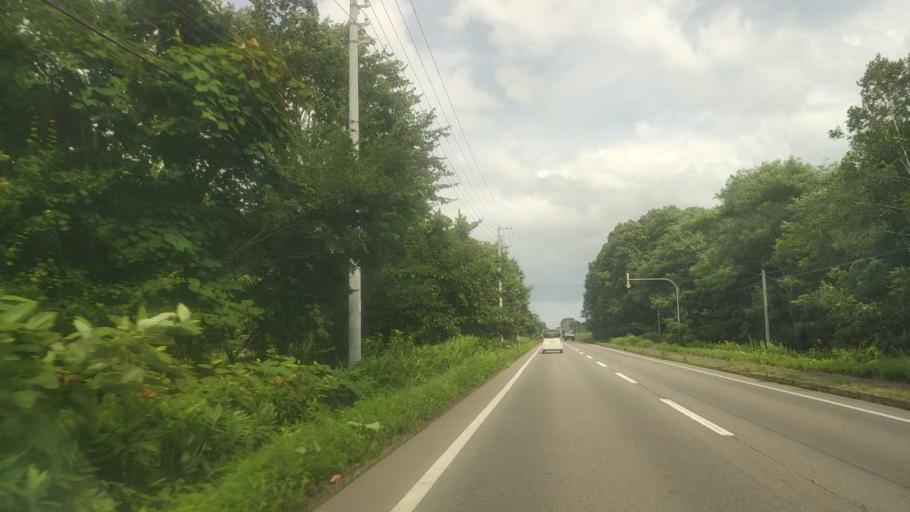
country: JP
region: Hokkaido
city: Nanae
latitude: 42.0305
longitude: 140.6100
